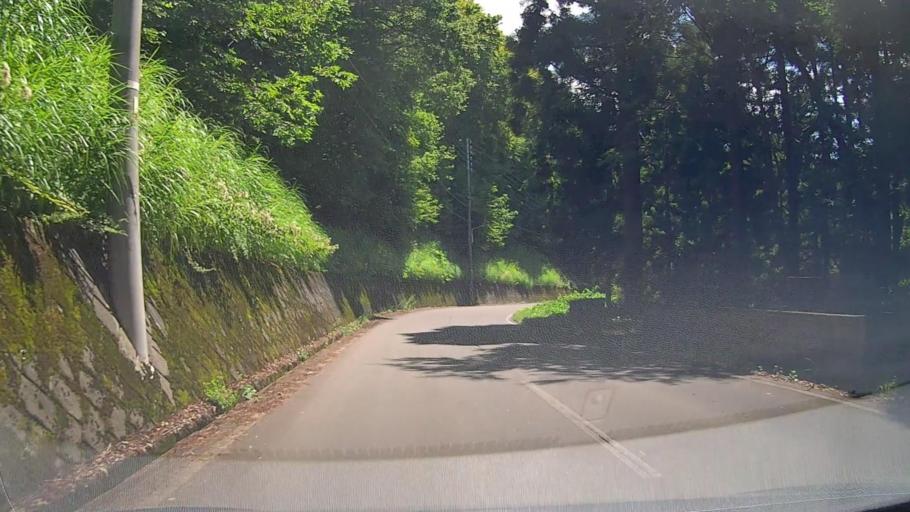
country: JP
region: Nagano
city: Iiyama
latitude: 36.9242
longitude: 138.4515
